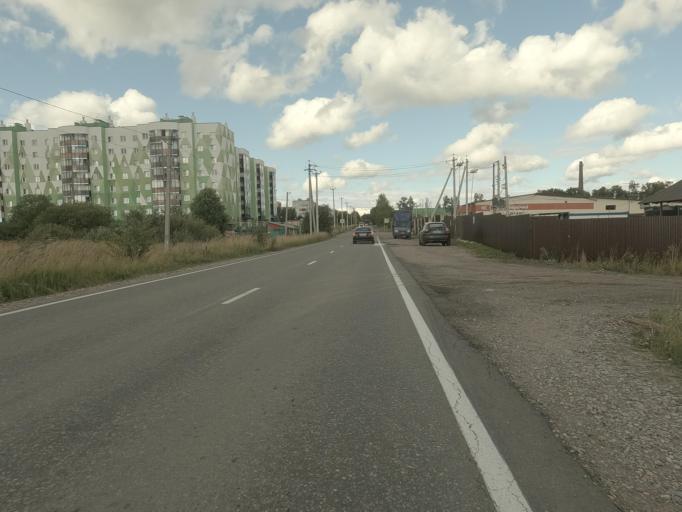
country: RU
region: Leningrad
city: Shcheglovo
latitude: 60.0235
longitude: 30.7495
